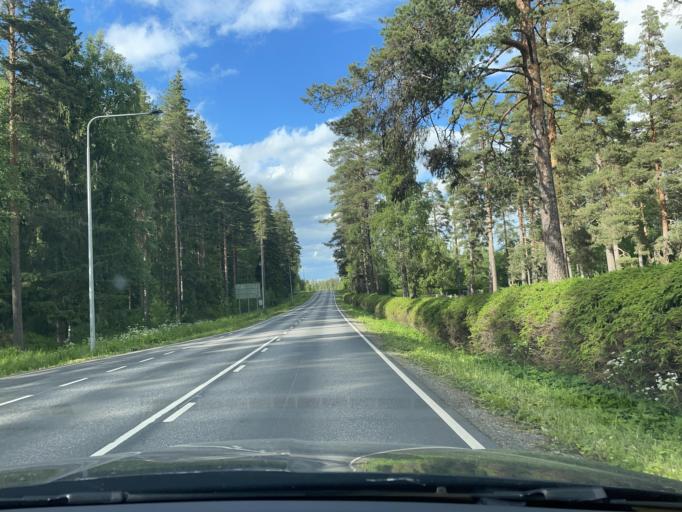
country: FI
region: Central Finland
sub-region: Jaemsae
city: Jaemsaenkoski
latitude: 62.0832
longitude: 25.1439
